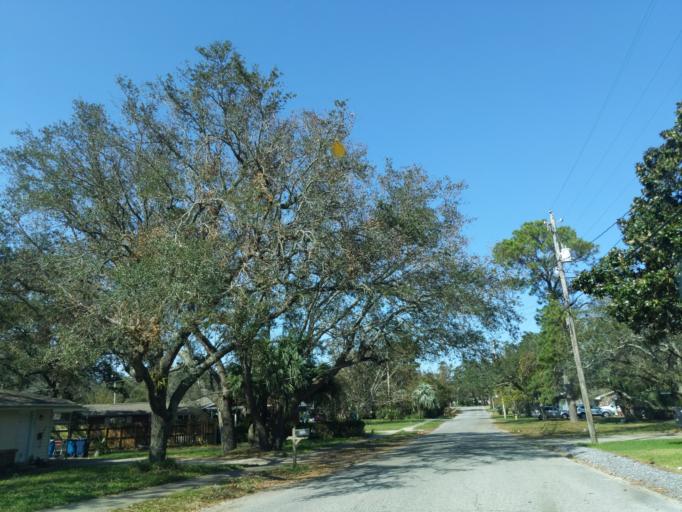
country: US
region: Florida
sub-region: Santa Rosa County
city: Gulf Breeze
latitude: 30.3585
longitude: -87.1861
